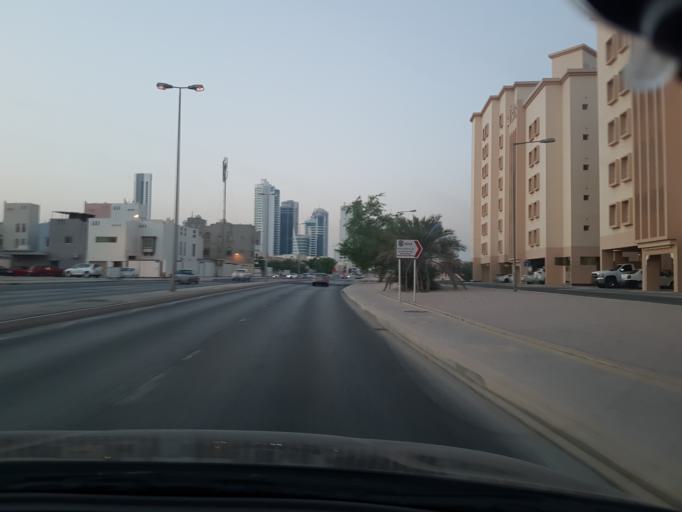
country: BH
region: Manama
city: Jidd Hafs
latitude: 26.2232
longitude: 50.5518
